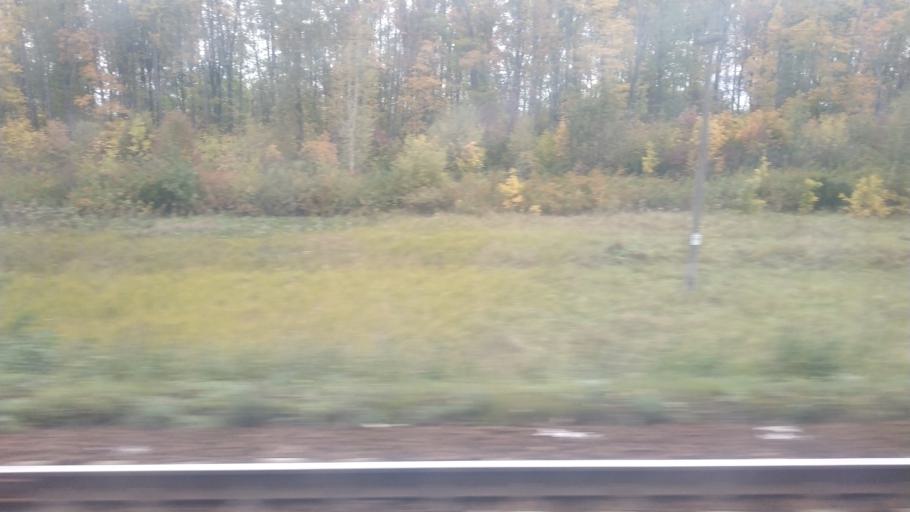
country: RU
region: Moskovskaya
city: Ozherel'ye
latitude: 54.7555
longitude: 38.3358
